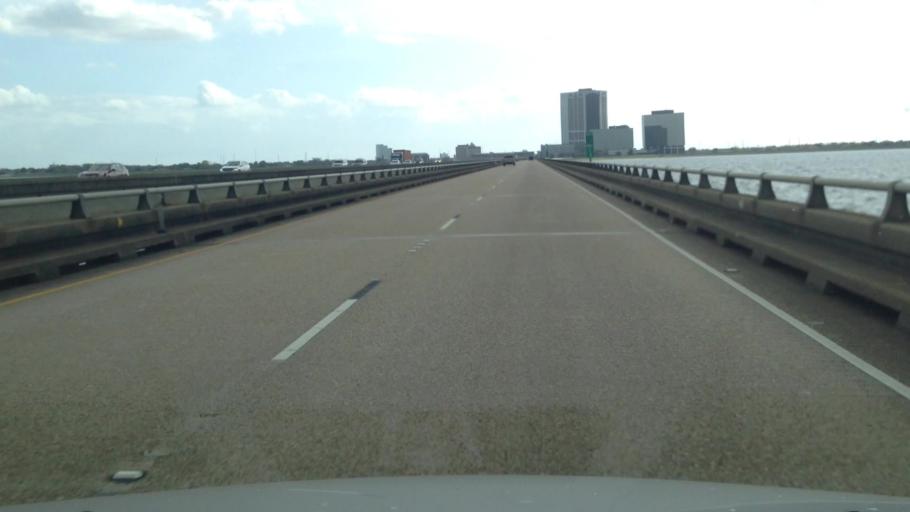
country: US
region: Louisiana
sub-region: Jefferson Parish
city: Metairie
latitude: 30.0337
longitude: -90.1520
